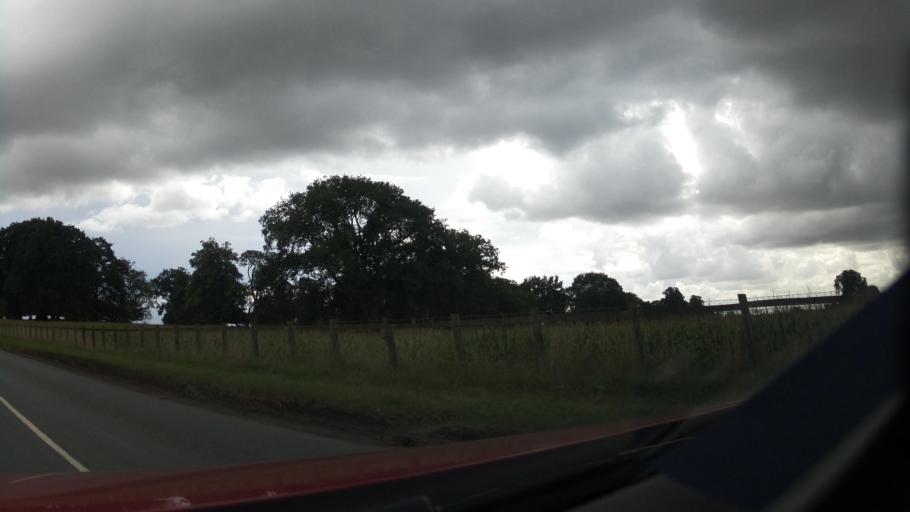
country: GB
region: England
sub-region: Staffordshire
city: Eccleshall
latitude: 52.9114
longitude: -2.2230
